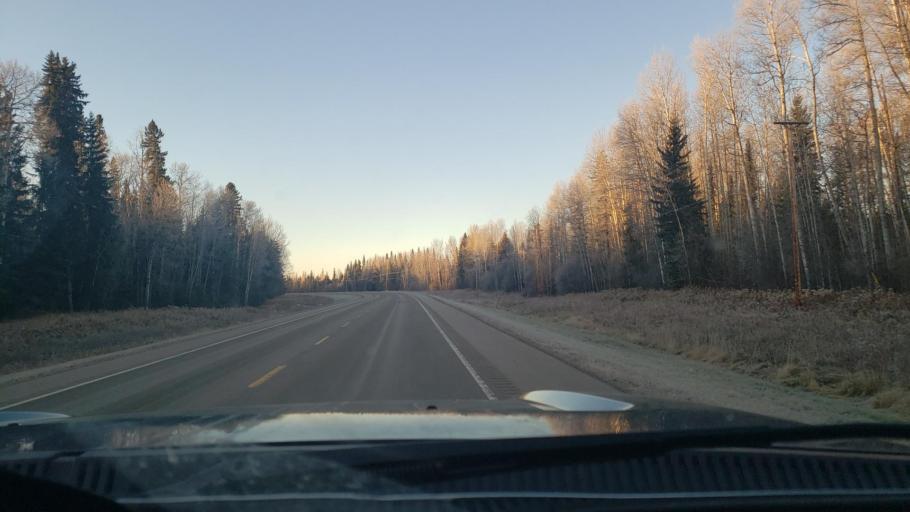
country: CA
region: British Columbia
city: Fort Nelson
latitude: 58.7075
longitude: -122.7121
